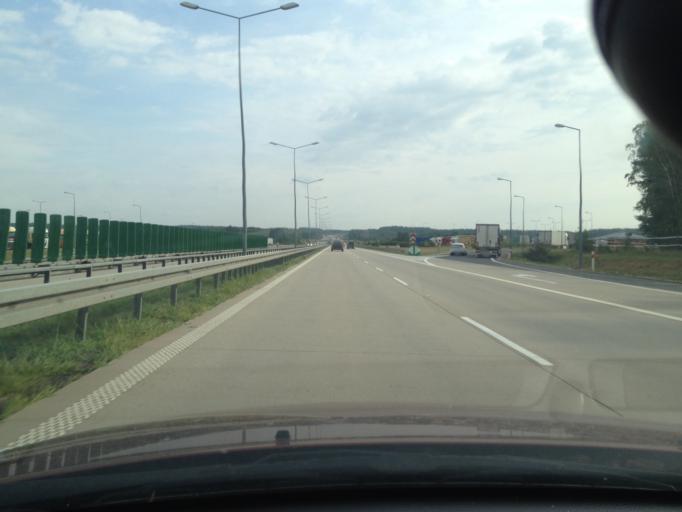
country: PL
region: Lower Silesian Voivodeship
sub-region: Powiat boleslawiecki
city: Nowogrodziec
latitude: 51.2461
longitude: 15.3432
